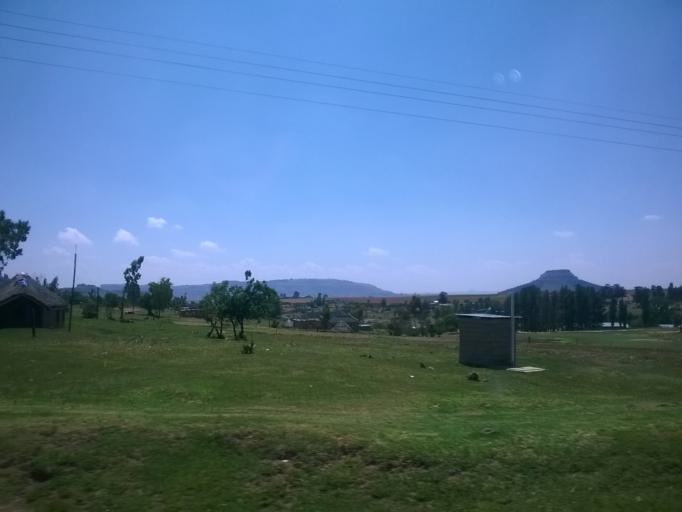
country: LS
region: Leribe
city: Maputsoe
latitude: -28.9722
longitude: 27.9726
